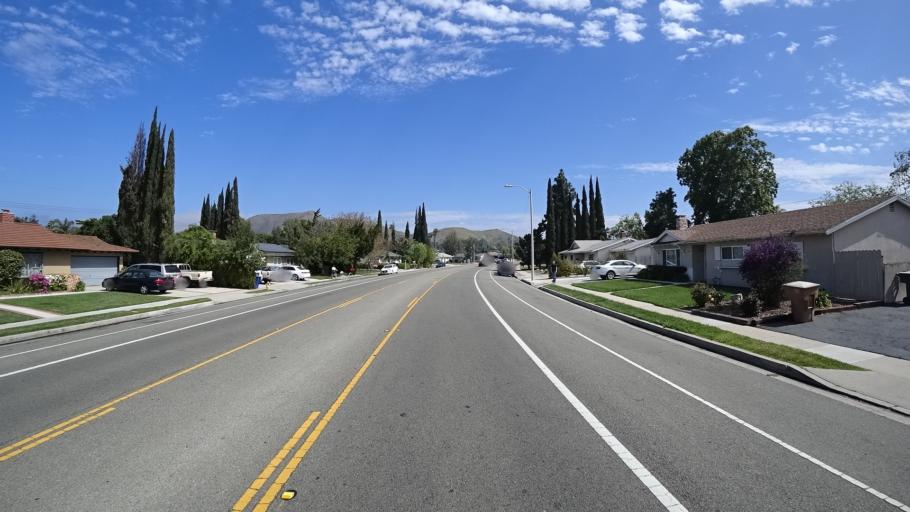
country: US
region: California
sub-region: Ventura County
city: Casa Conejo
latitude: 34.1851
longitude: -118.9447
